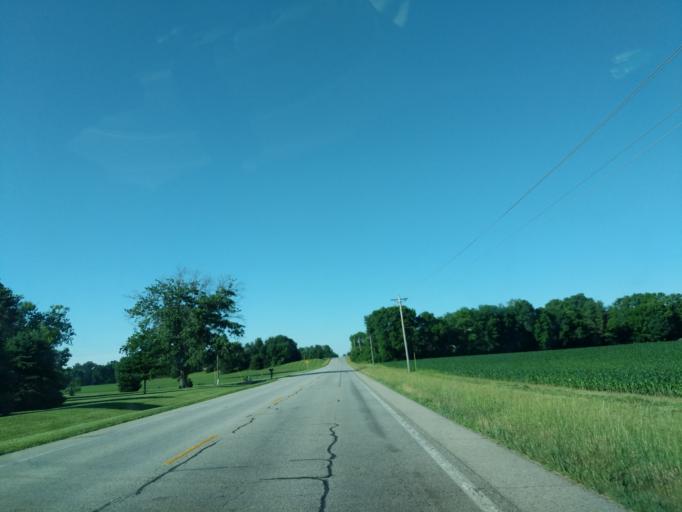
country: US
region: Indiana
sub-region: Shelby County
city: Shelbyville
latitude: 39.6080
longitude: -85.7693
